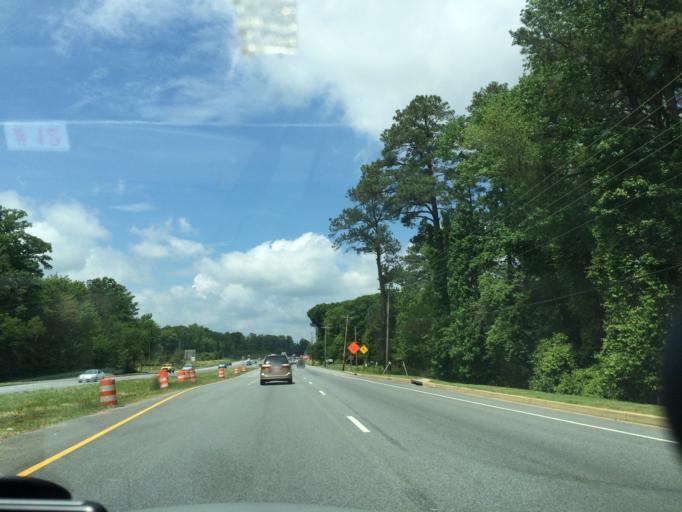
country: US
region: Maryland
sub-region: Saint Mary's County
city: California
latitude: 38.3054
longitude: -76.5238
